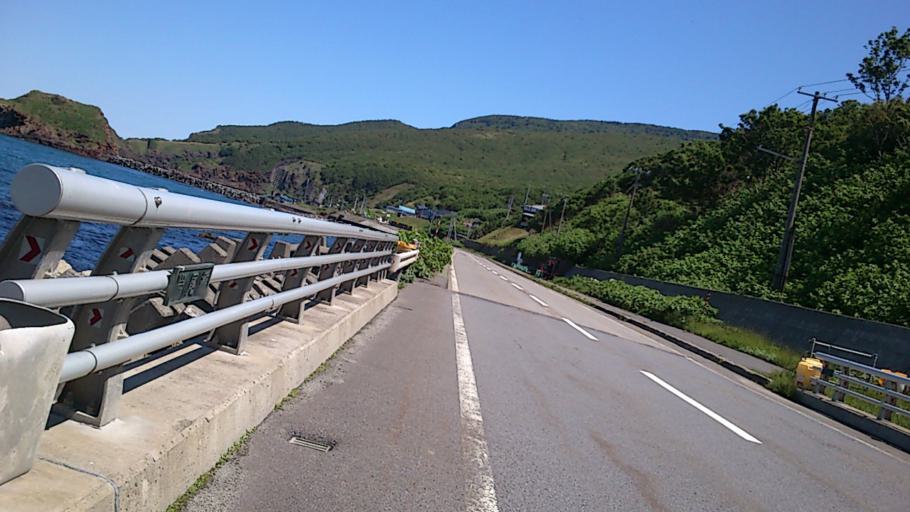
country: JP
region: Hokkaido
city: Rumoi
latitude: 43.7707
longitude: 141.3659
